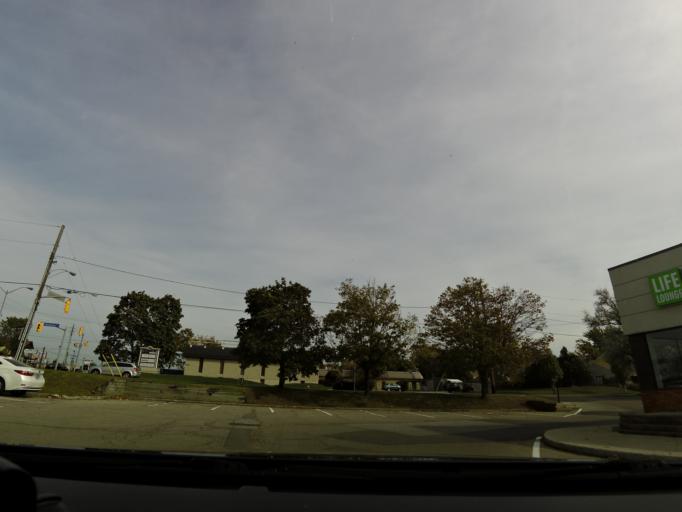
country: CA
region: Ontario
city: Burlington
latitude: 43.3551
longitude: -79.7838
